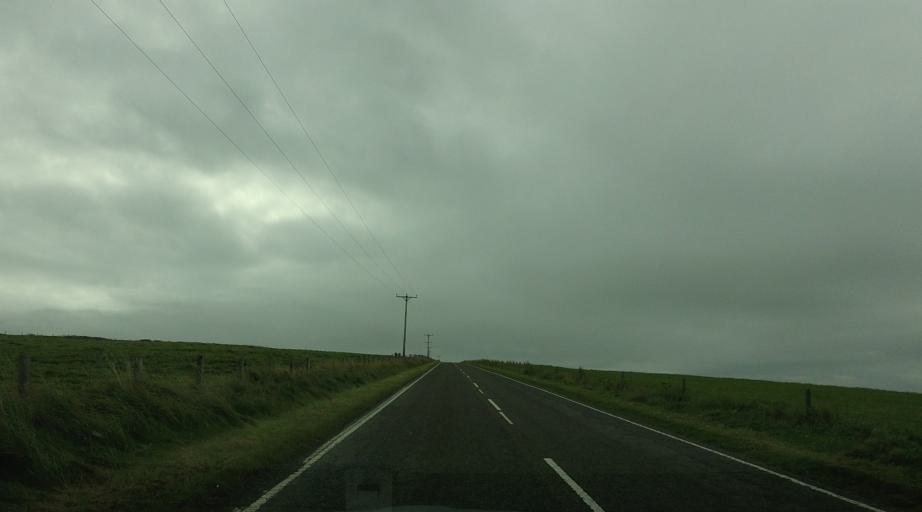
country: GB
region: Scotland
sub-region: Orkney Islands
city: Orkney
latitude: 58.7785
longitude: -2.9599
